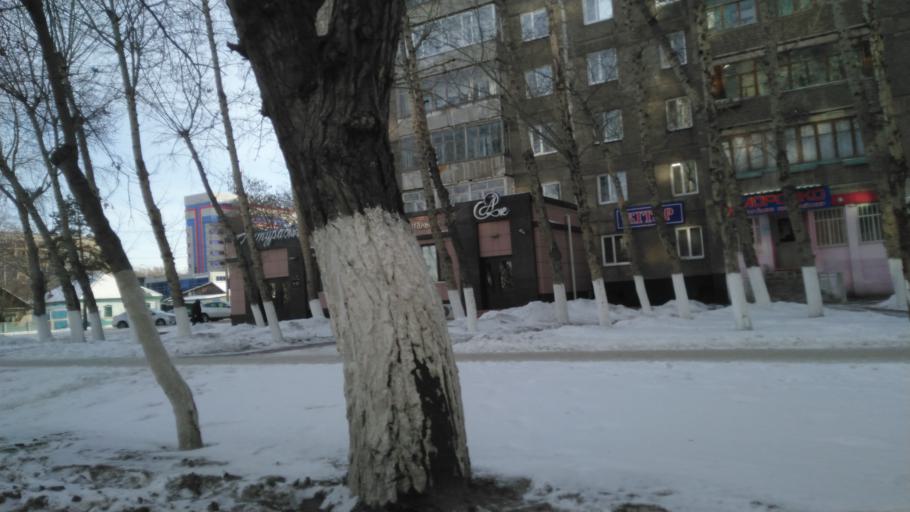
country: KZ
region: Pavlodar
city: Pavlodar
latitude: 52.2678
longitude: 76.9530
